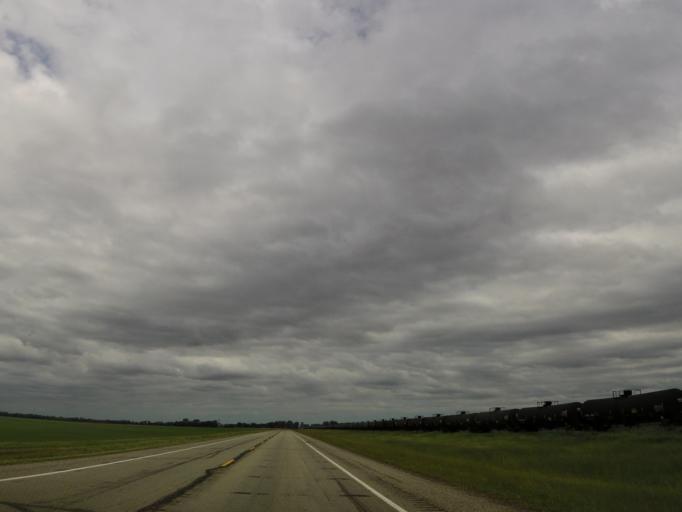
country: US
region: North Dakota
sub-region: Walsh County
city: Grafton
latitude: 48.4927
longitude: -97.4337
